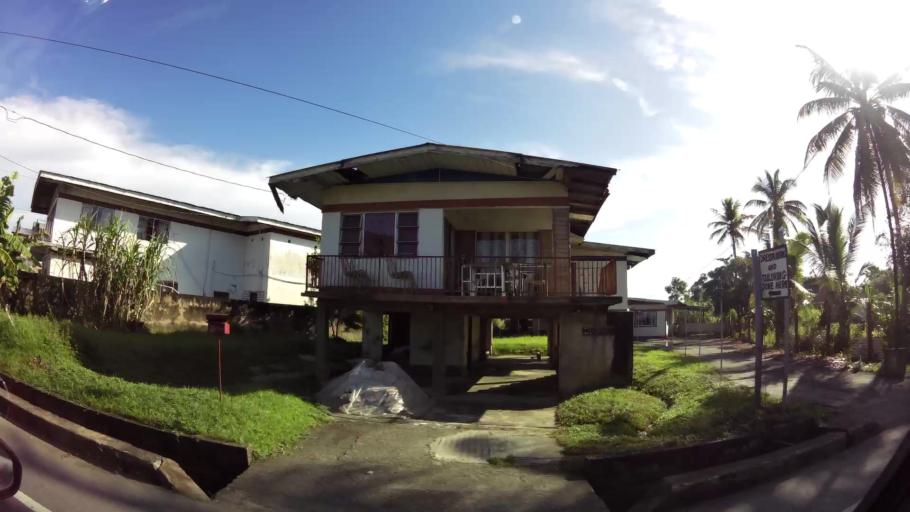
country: TT
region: Chaguanas
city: Chaguanas
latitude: 10.5145
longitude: -61.3781
